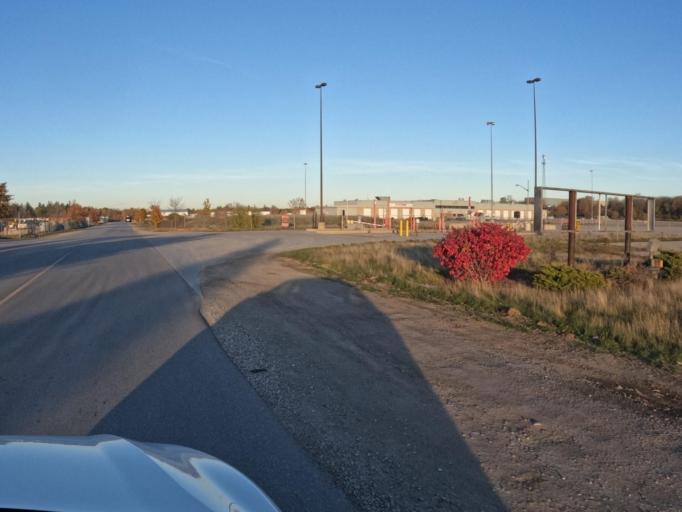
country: CA
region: Ontario
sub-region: Wellington County
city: Guelph
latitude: 43.4623
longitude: -80.1336
